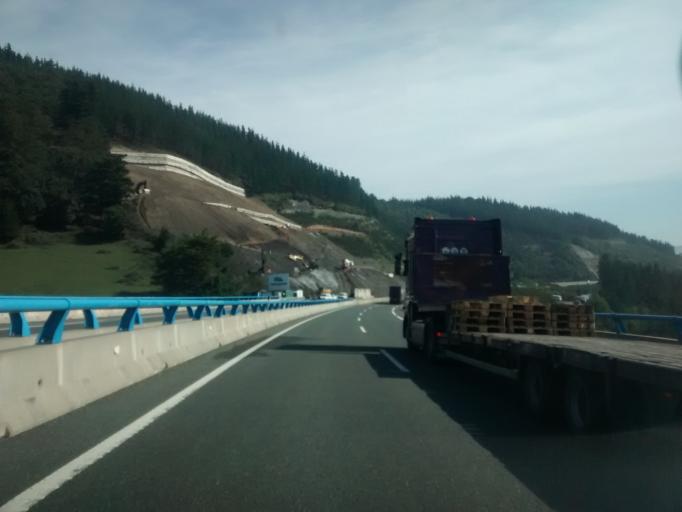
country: ES
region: Basque Country
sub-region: Provincia de Guipuzcoa
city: Eskoriatza
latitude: 43.0156
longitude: -2.5507
